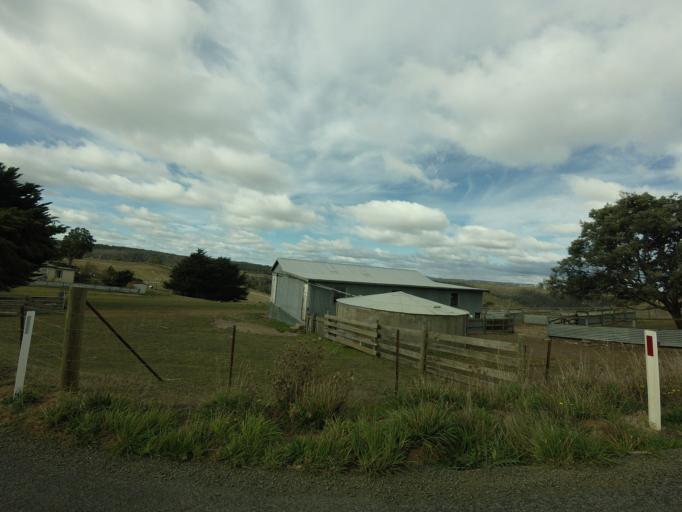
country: AU
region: Tasmania
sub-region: Brighton
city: Bridgewater
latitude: -42.4307
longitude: 147.3862
